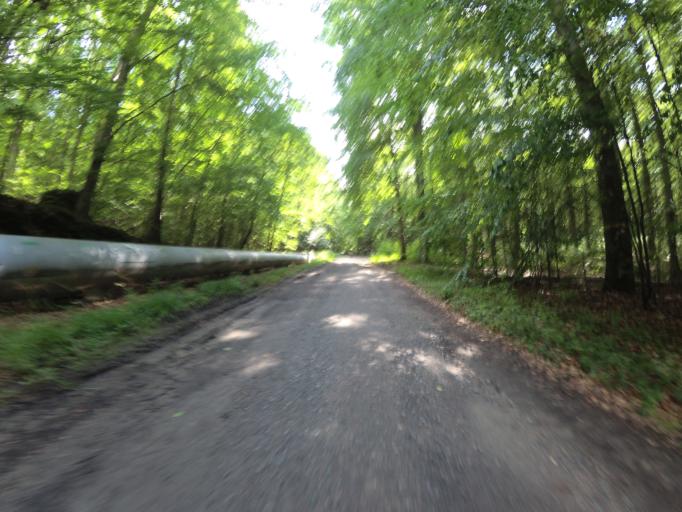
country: PL
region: Pomeranian Voivodeship
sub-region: Gdynia
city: Wielki Kack
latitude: 54.5090
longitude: 18.4881
